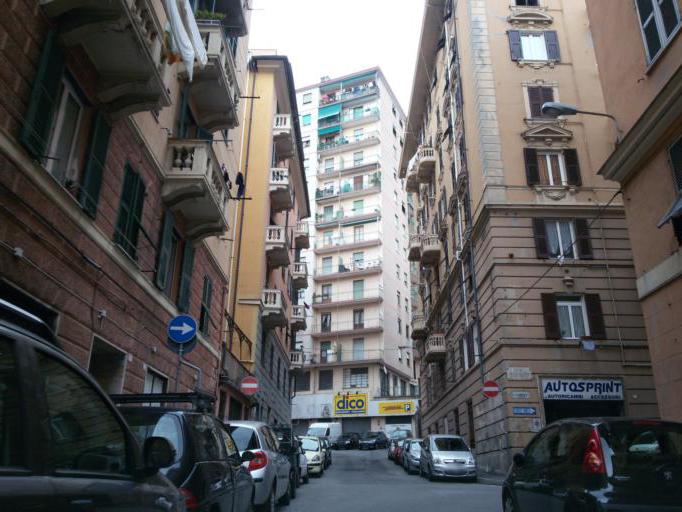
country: IT
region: Liguria
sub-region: Provincia di Genova
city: San Teodoro
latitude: 44.4145
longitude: 8.8902
